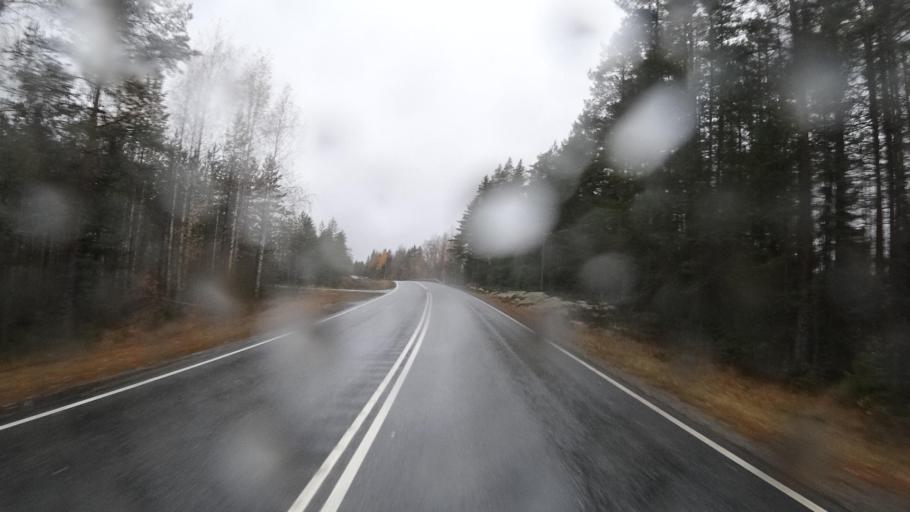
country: FI
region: Northern Savo
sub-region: Koillis-Savo
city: Tuusniemi
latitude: 62.8687
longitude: 28.4114
